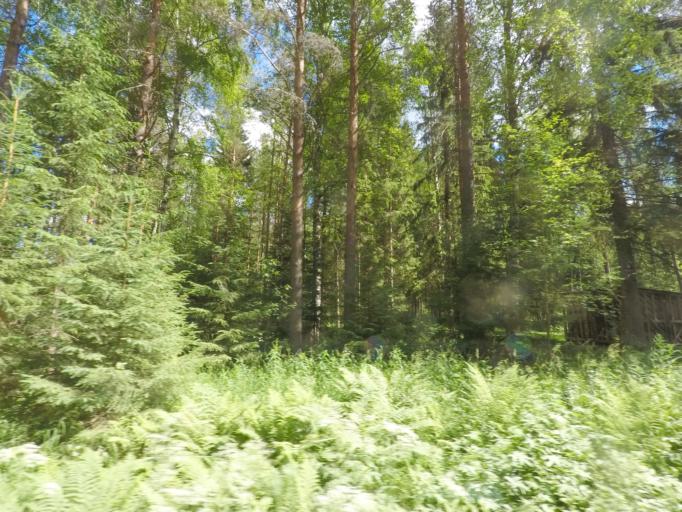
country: FI
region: Central Finland
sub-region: Jyvaeskylae
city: Hankasalmi
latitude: 62.4362
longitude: 26.6473
